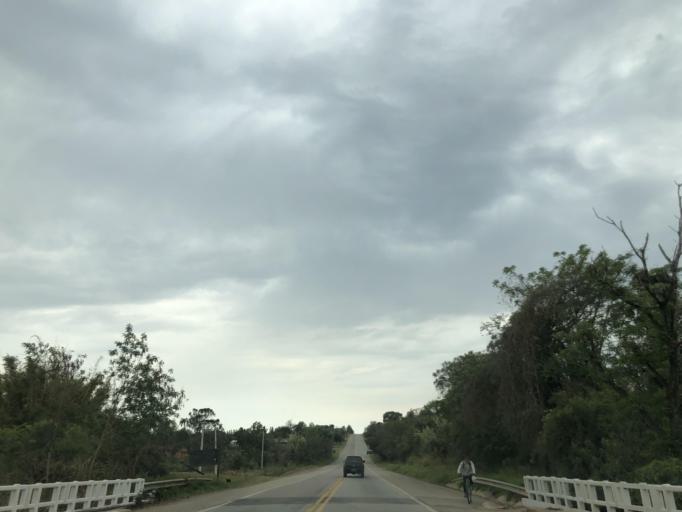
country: BR
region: Sao Paulo
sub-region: Salto De Pirapora
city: Salto de Pirapora
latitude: -23.7072
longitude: -47.6321
